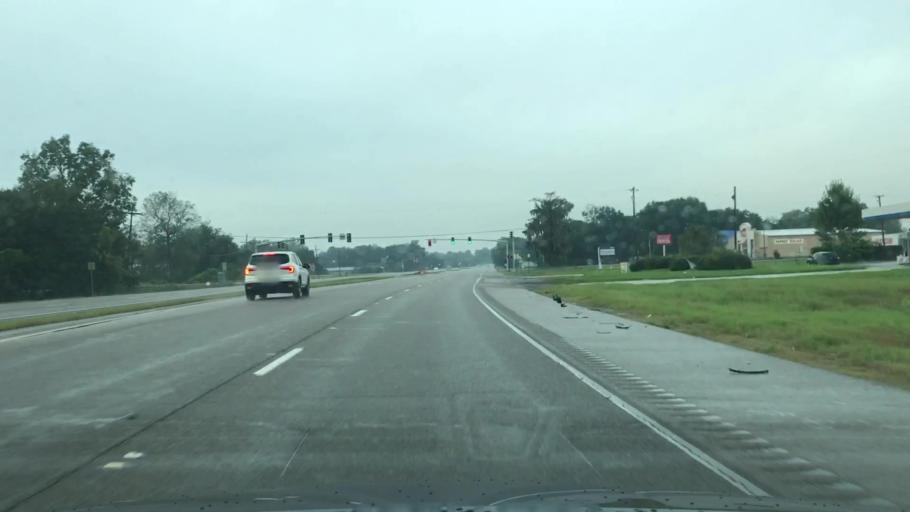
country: US
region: Louisiana
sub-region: Saint Charles Parish
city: Des Allemands
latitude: 29.8253
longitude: -90.4643
